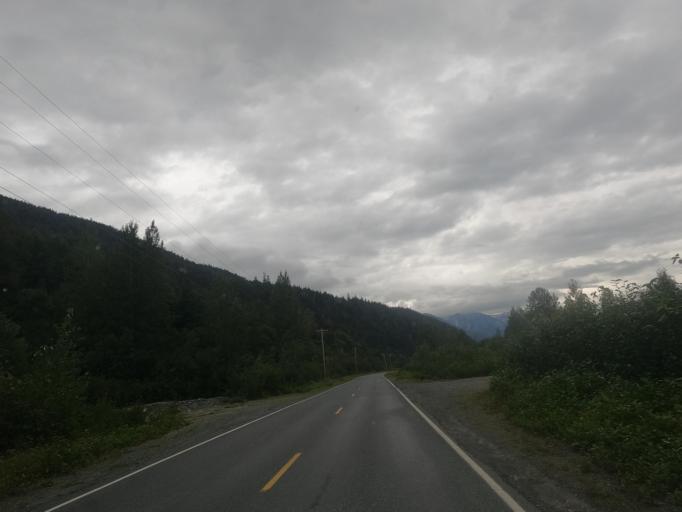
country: US
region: Alaska
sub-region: Haines Borough
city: Haines
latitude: 59.2835
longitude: -135.4730
